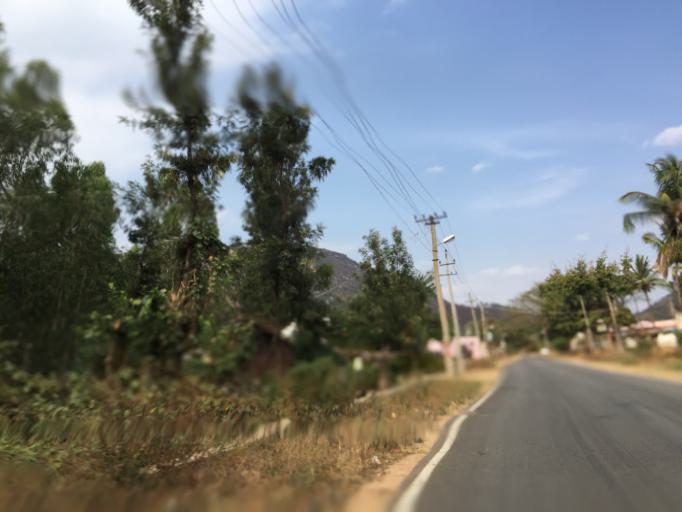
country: IN
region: Karnataka
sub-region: Chikkaballapur
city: Chik Ballapur
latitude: 13.3669
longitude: 77.6595
